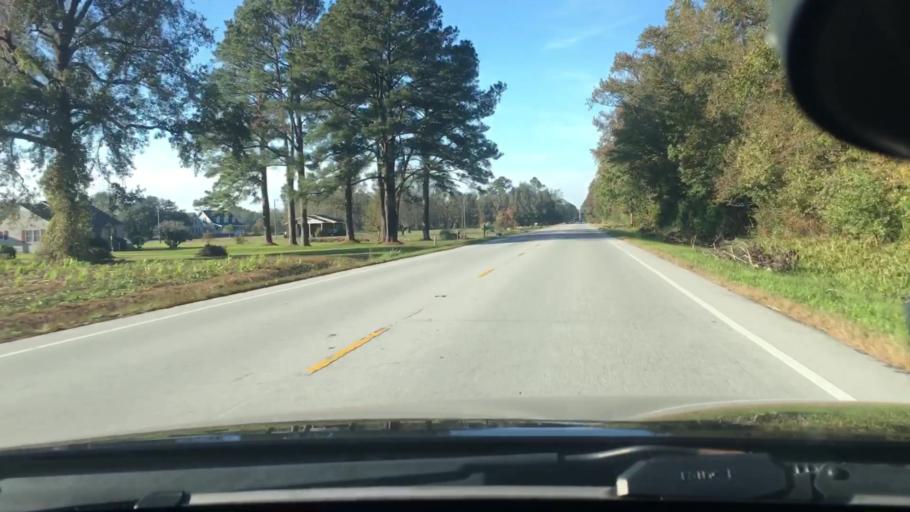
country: US
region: North Carolina
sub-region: Craven County
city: New Bern
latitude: 35.1693
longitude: -77.0424
